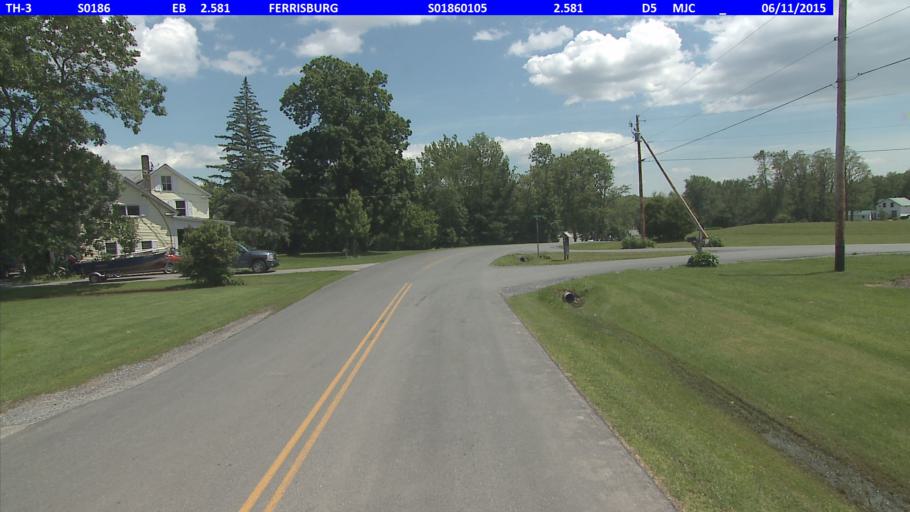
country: US
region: Vermont
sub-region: Addison County
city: Vergennes
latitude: 44.1882
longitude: -73.3147
